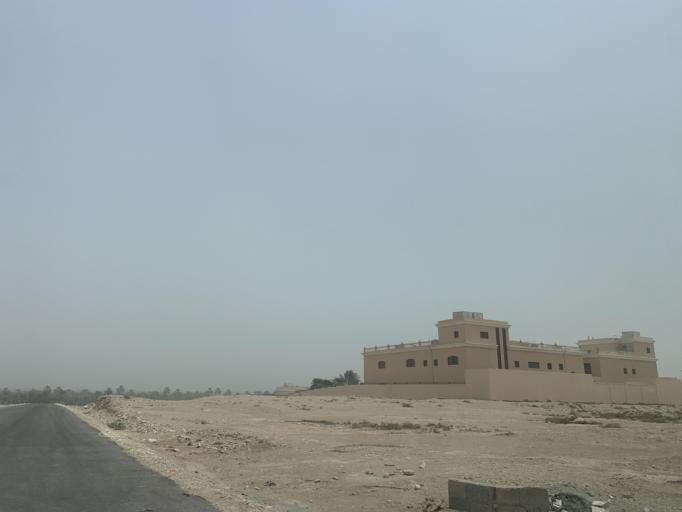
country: BH
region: Central Governorate
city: Madinat Hamad
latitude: 26.1680
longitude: 50.4817
